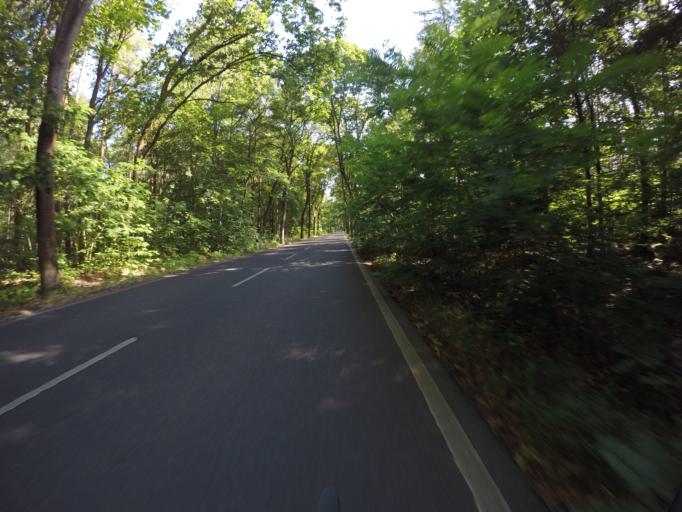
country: DE
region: Berlin
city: Schmockwitz
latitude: 52.3574
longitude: 13.6504
